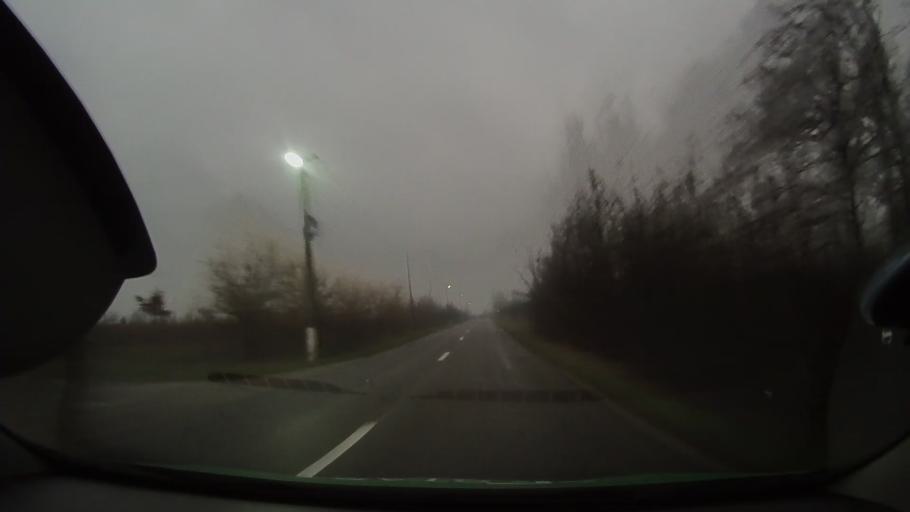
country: RO
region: Arad
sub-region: Comuna Beliu
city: Beliu
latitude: 46.5008
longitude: 21.9737
